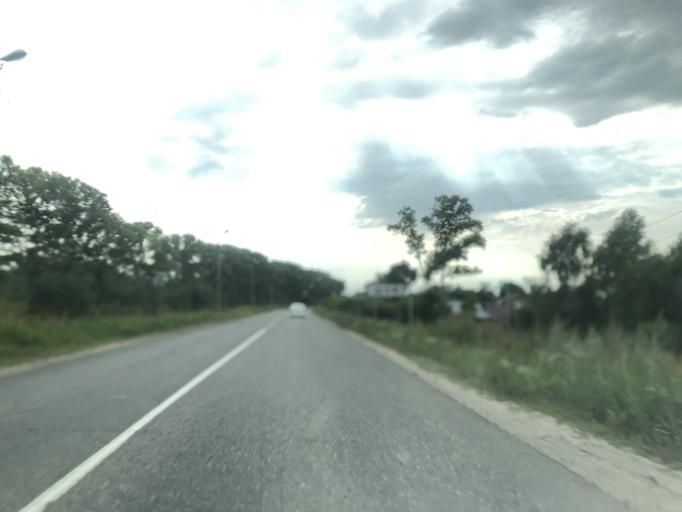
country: RU
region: Ivanovo
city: Shuya
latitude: 56.8561
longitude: 41.4328
